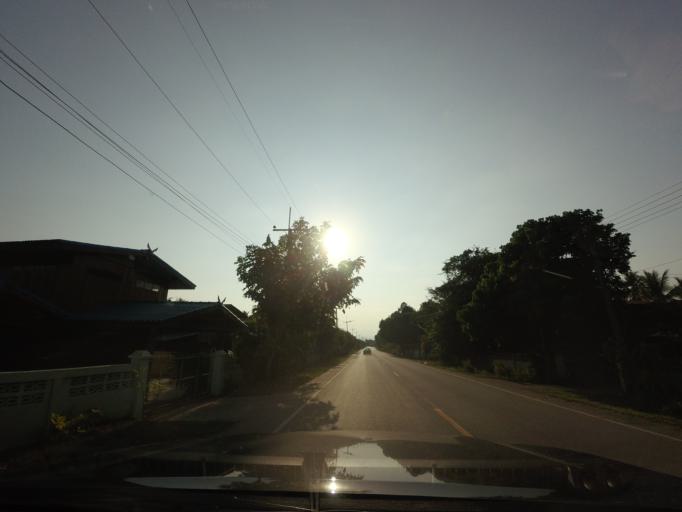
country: TH
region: Nan
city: Na Noi
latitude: 18.3347
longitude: 100.7729
